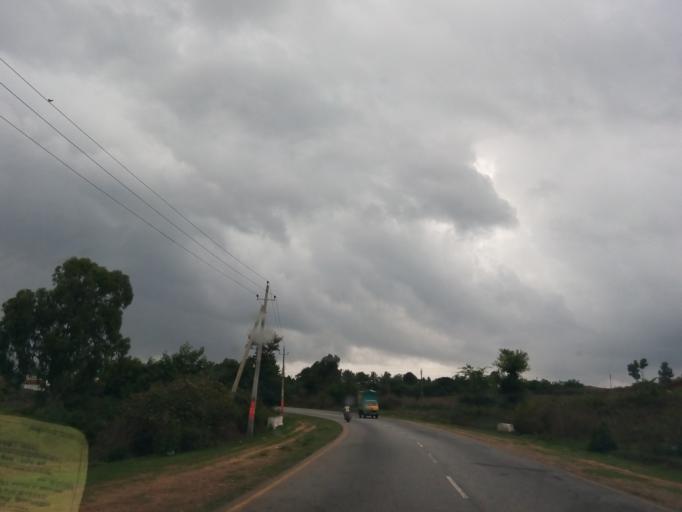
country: IN
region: Karnataka
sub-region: Hassan
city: Hassan
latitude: 13.0970
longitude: 76.0257
